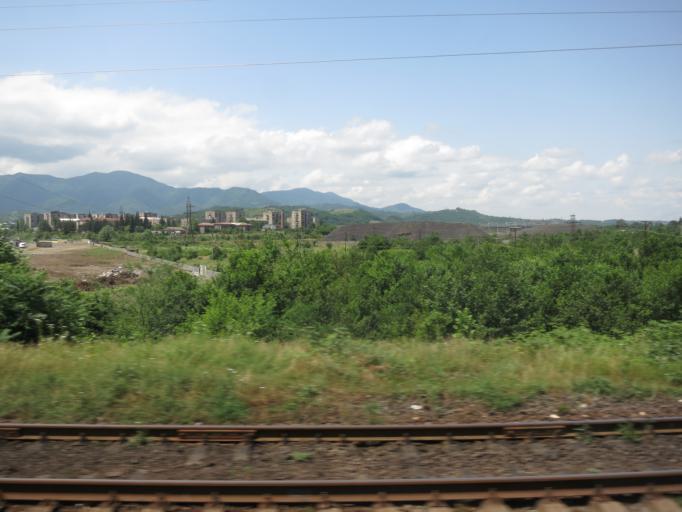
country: GE
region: Imereti
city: Zestap'oni
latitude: 42.1138
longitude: 43.0218
